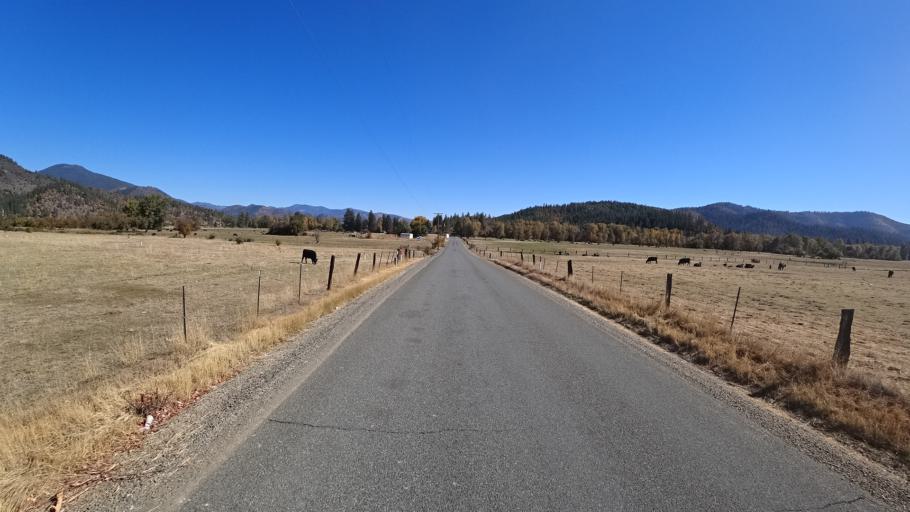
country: US
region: California
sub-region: Siskiyou County
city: Yreka
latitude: 41.6241
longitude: -122.9723
